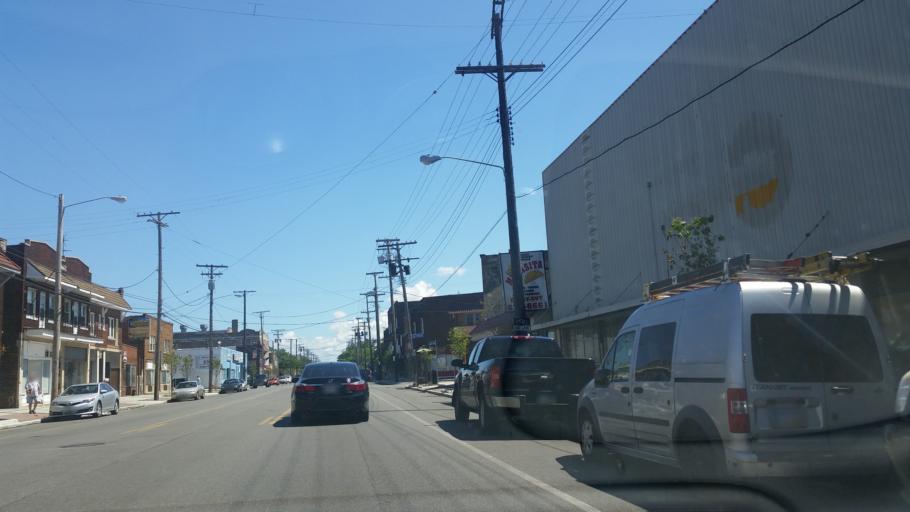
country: US
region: Ohio
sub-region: Cuyahoga County
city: Lakewood
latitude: 41.4603
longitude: -81.7737
